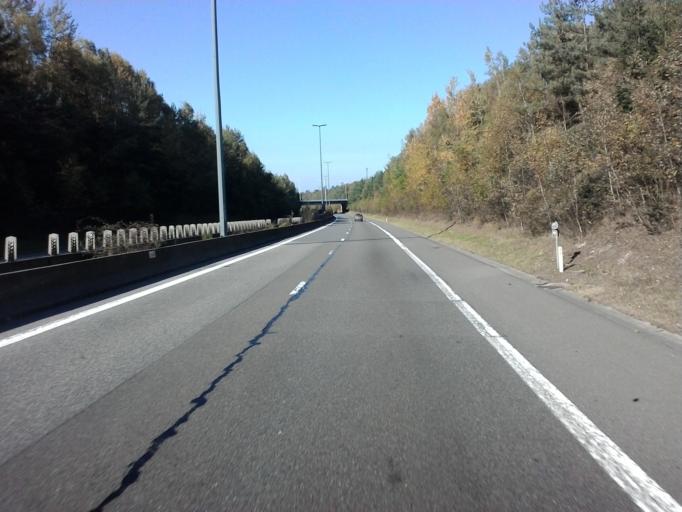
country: BE
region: Wallonia
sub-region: Province du Luxembourg
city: Tellin
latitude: 50.0482
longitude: 5.2116
